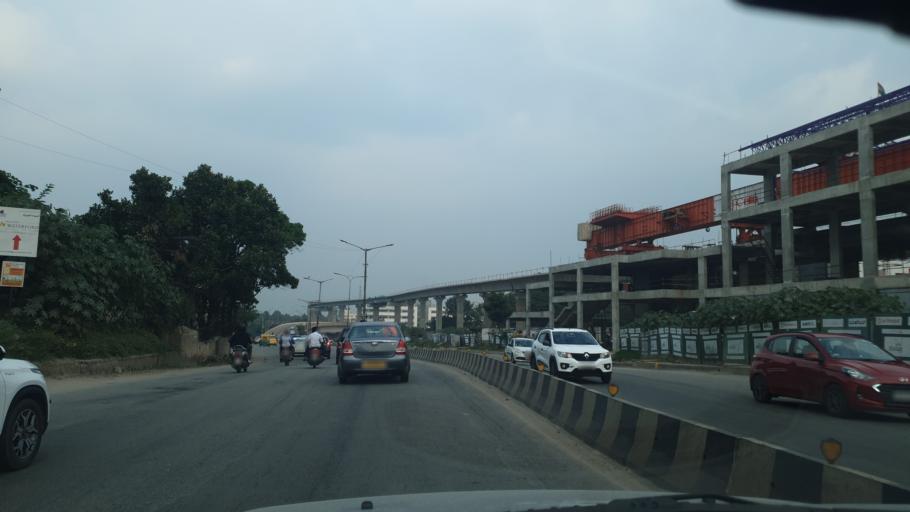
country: IN
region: Karnataka
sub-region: Bangalore Urban
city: Bangalore
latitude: 13.0004
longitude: 77.6777
